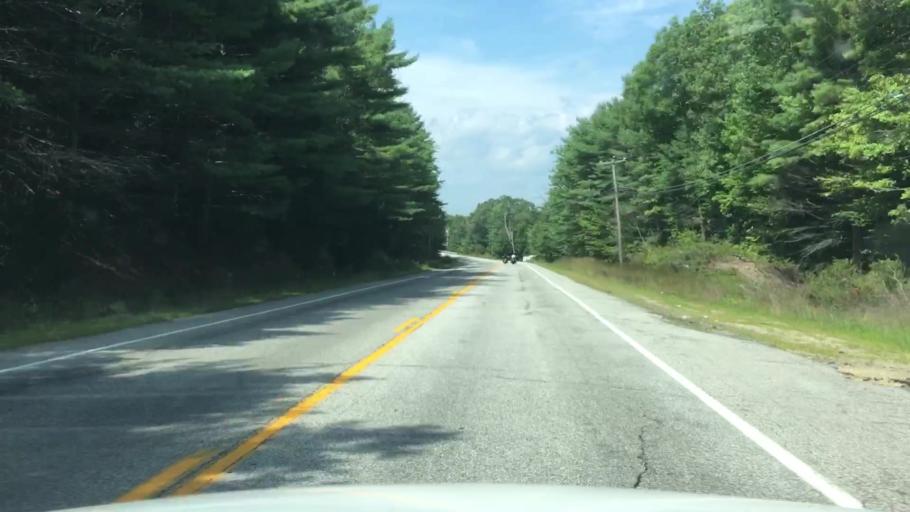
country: US
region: Maine
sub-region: Oxford County
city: Peru
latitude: 44.4930
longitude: -70.3857
